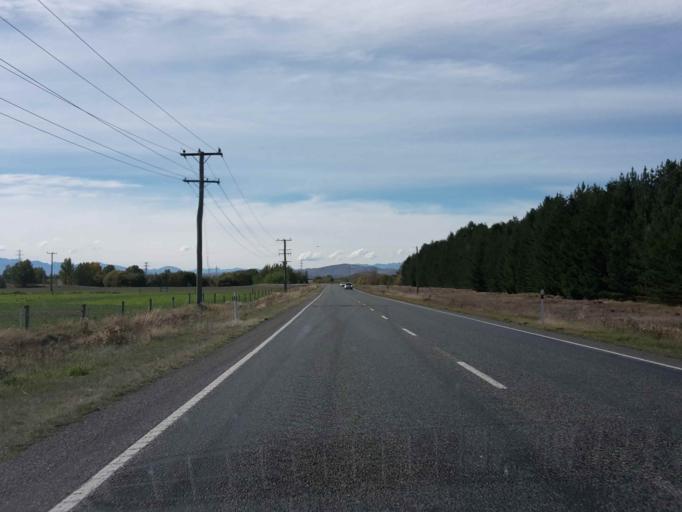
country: NZ
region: Otago
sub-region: Queenstown-Lakes District
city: Wanaka
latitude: -44.3069
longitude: 170.0627
